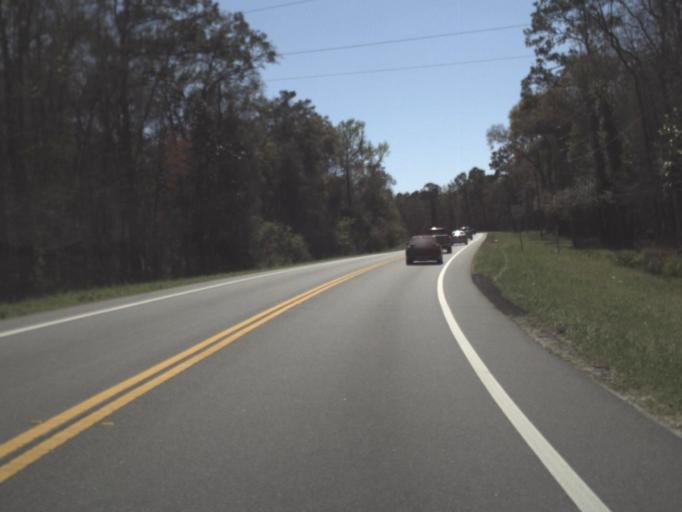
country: US
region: Florida
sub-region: Gadsden County
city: Midway
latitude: 30.4912
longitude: -84.3617
